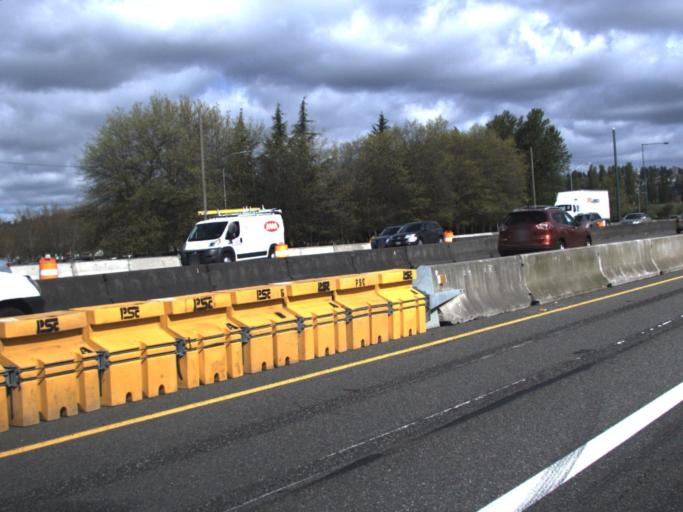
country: US
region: Washington
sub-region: King County
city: Tukwila
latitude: 47.4624
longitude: -122.2614
